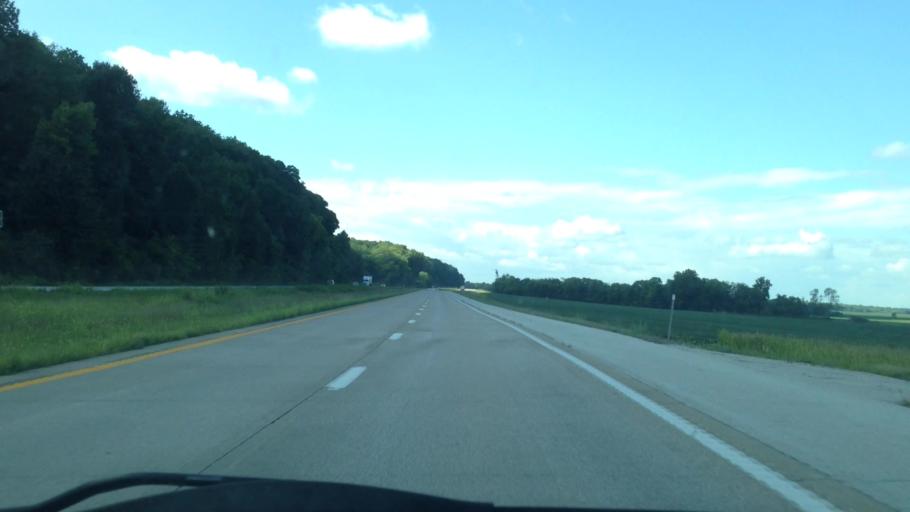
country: US
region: Missouri
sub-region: Lewis County
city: Canton
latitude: 40.2229
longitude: -91.5272
